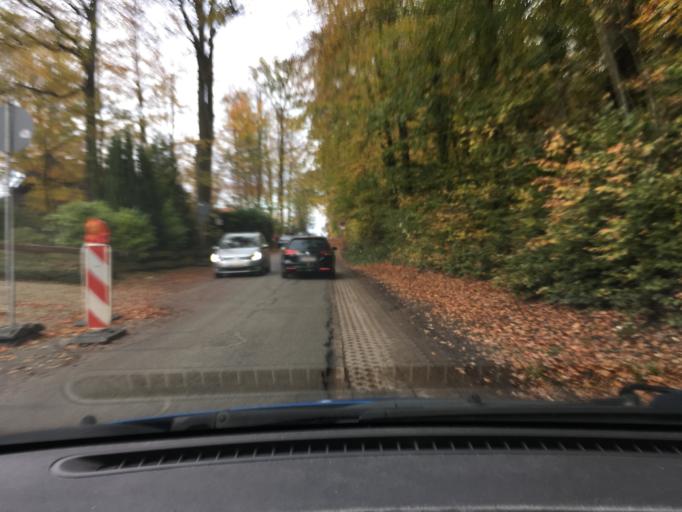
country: DE
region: Lower Saxony
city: Seevetal
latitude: 53.4136
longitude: 9.9896
